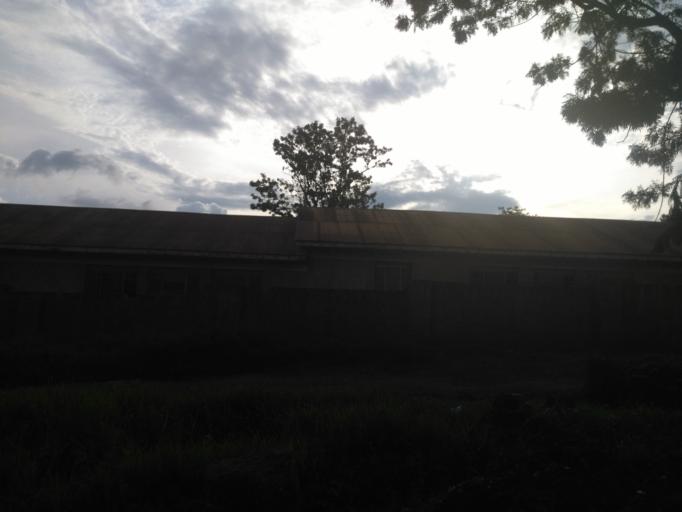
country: UG
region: Eastern Region
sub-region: Jinja District
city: Jinja
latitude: 0.4348
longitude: 33.2137
